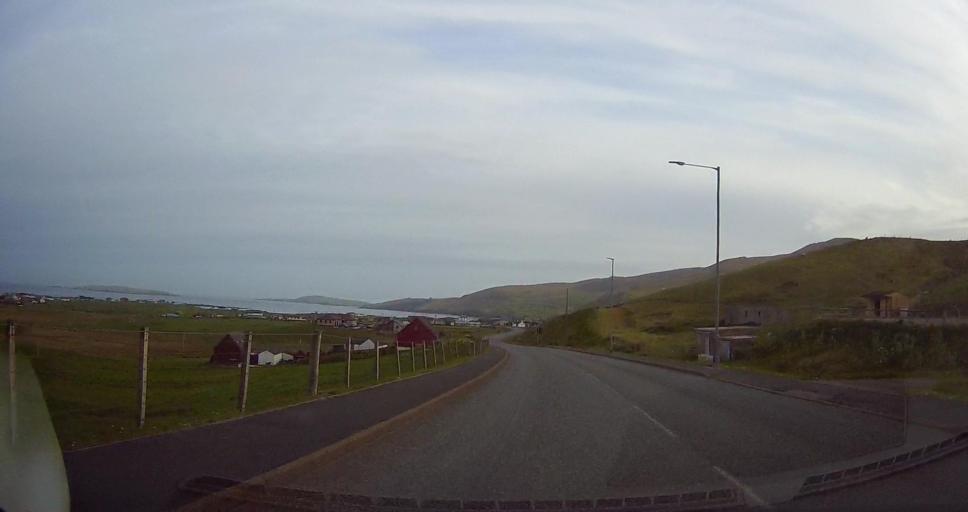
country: GB
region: Scotland
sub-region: Shetland Islands
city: Sandwick
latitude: 60.0445
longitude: -1.2286
